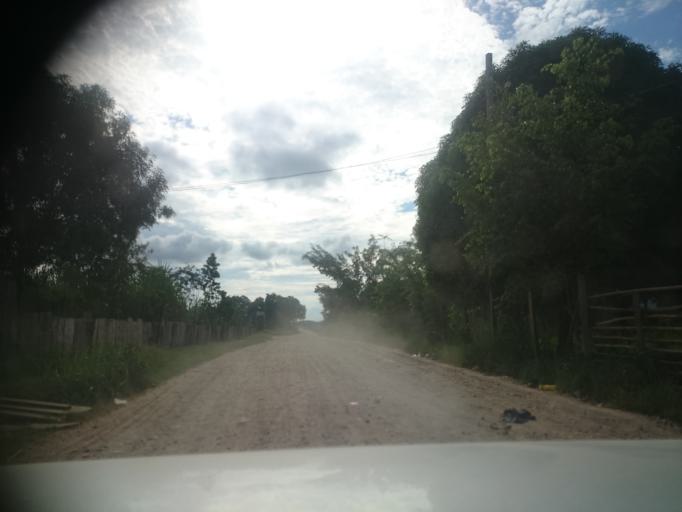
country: PE
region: Ucayali
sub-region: Provincia de Coronel Portillo
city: Puerto Callao
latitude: -8.3728
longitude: -74.5989
